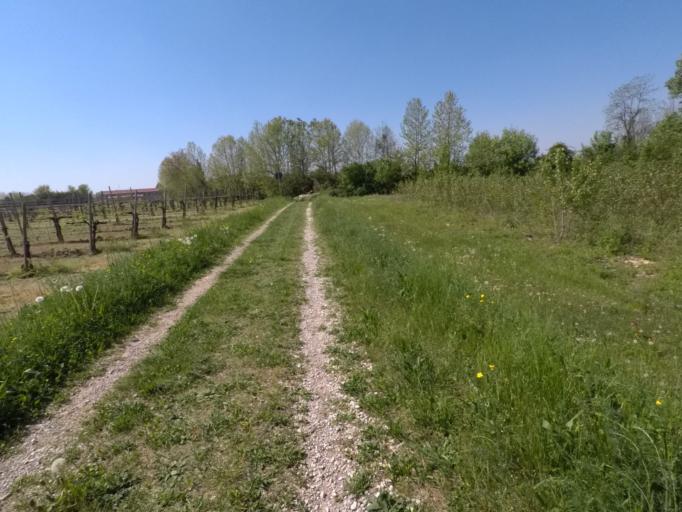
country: IT
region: Veneto
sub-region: Provincia di Treviso
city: Portobuffole
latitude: 45.8675
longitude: 12.5368
